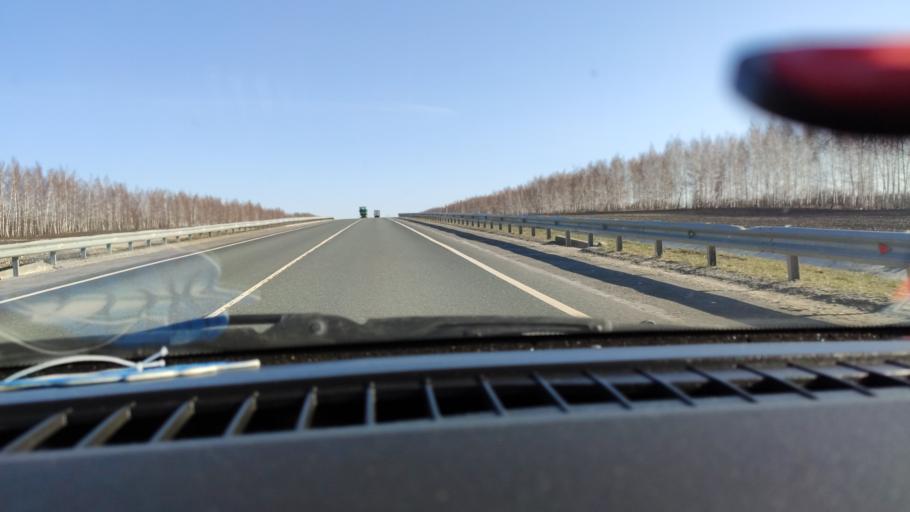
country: RU
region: Samara
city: Syzran'
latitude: 52.9036
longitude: 48.2978
